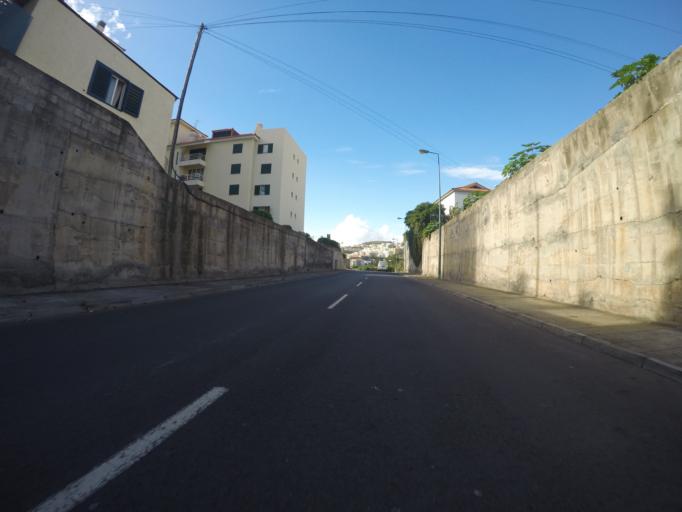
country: PT
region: Madeira
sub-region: Funchal
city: Nossa Senhora do Monte
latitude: 32.6538
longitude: -16.9243
